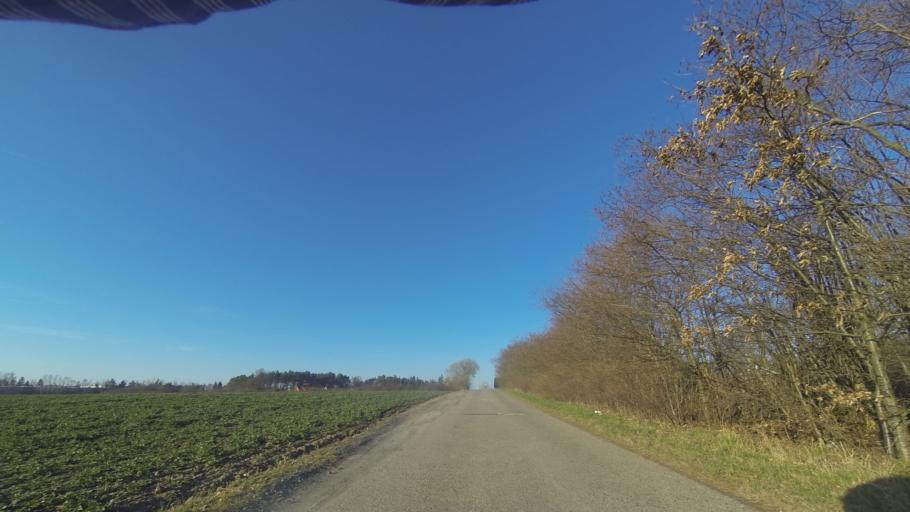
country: DE
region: Saxony
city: Ottendorf-Okrilla
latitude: 51.1782
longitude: 13.7828
